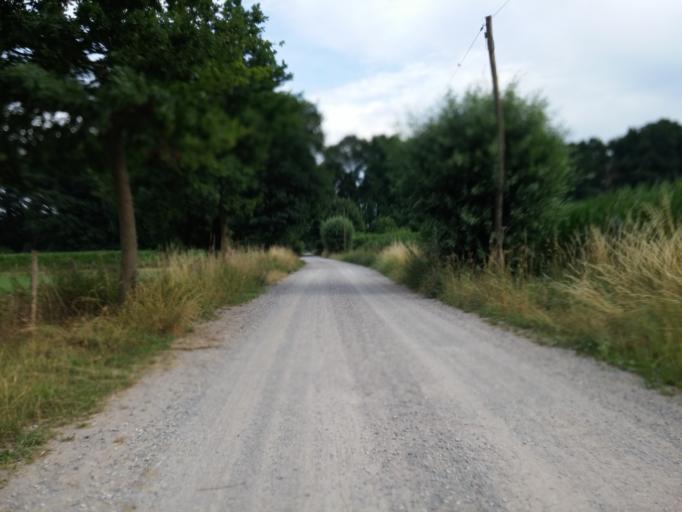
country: DE
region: North Rhine-Westphalia
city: Tonisvorst
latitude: 51.3884
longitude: 6.5237
